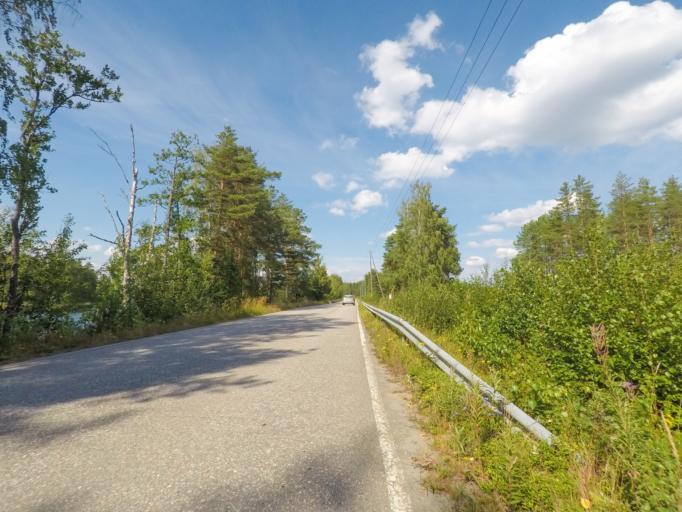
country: FI
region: Southern Savonia
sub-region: Mikkeli
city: Puumala
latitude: 61.4898
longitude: 28.1666
